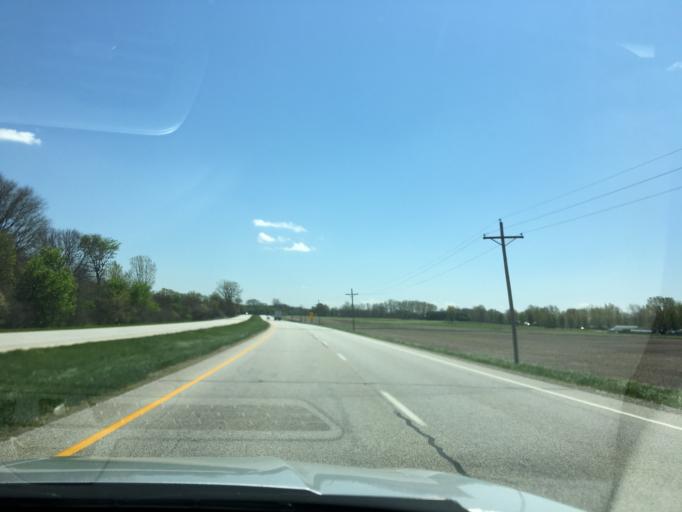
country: US
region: Indiana
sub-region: Boone County
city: Thorntown
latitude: 40.2212
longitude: -86.6650
